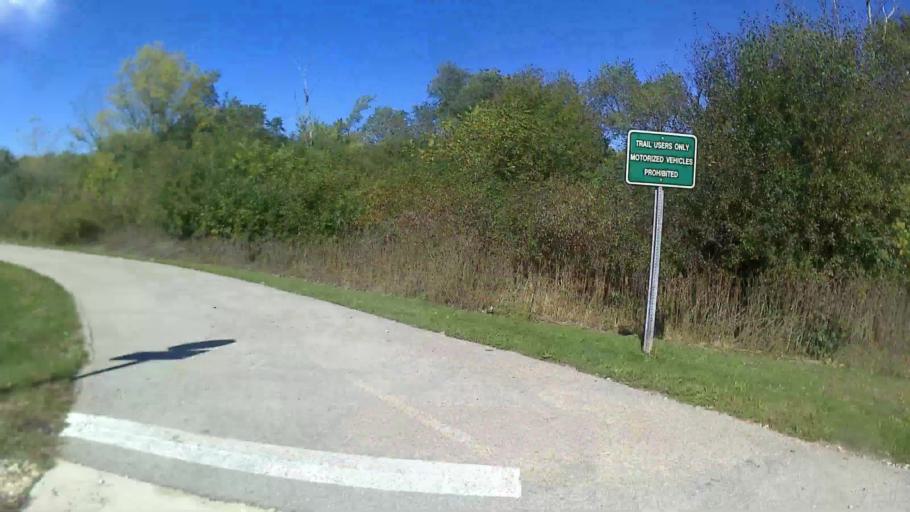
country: US
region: Illinois
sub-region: DuPage County
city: Itasca
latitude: 41.9598
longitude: -88.0051
